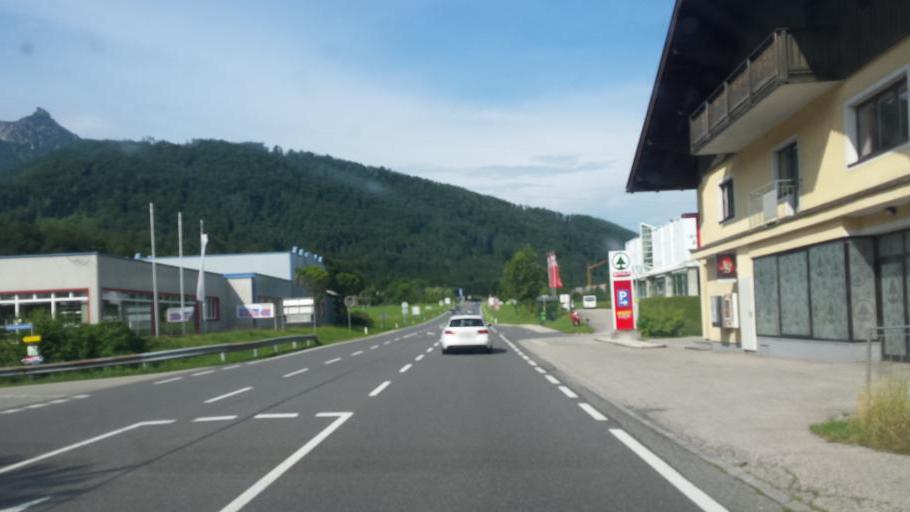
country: AT
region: Upper Austria
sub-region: Politischer Bezirk Gmunden
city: Bad Ischl
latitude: 47.7125
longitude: 13.5553
